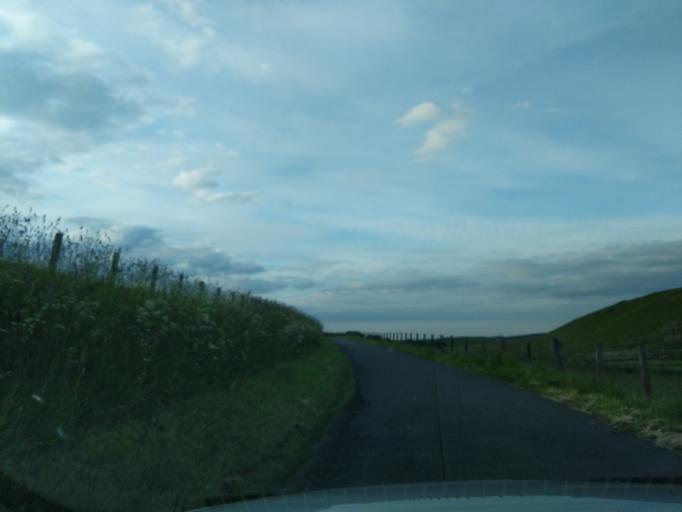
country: GB
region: Scotland
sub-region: Midlothian
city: Gorebridge
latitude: 55.7906
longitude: -3.0930
